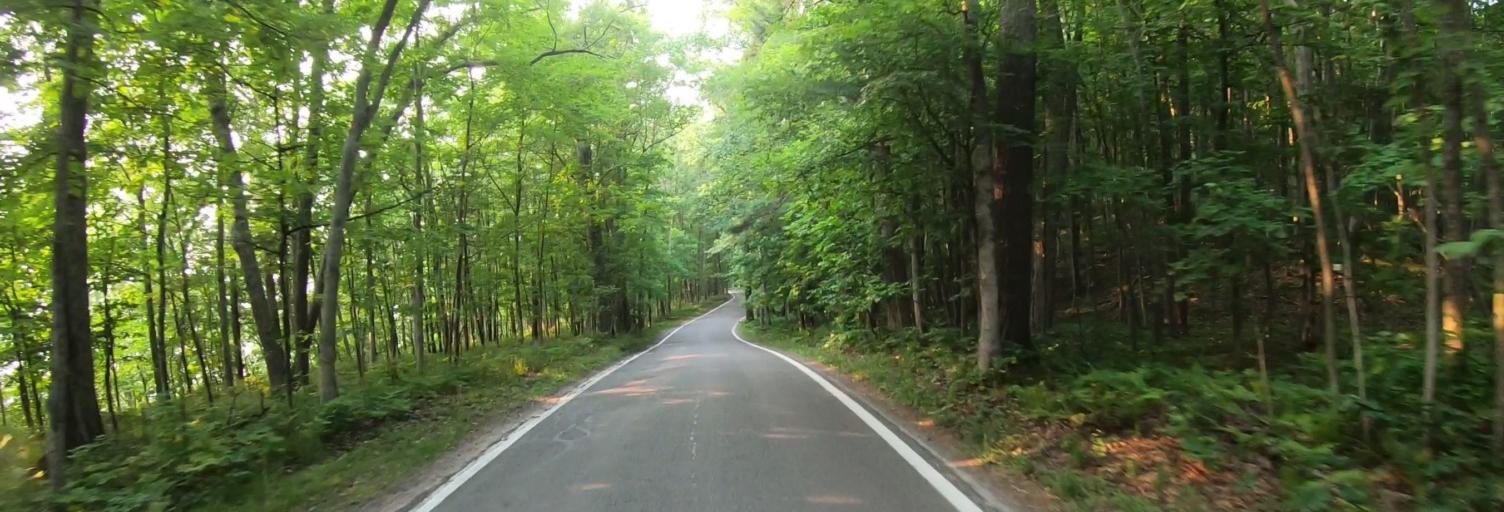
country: US
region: Michigan
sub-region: Emmet County
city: Harbor Springs
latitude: 45.5291
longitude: -85.1100
